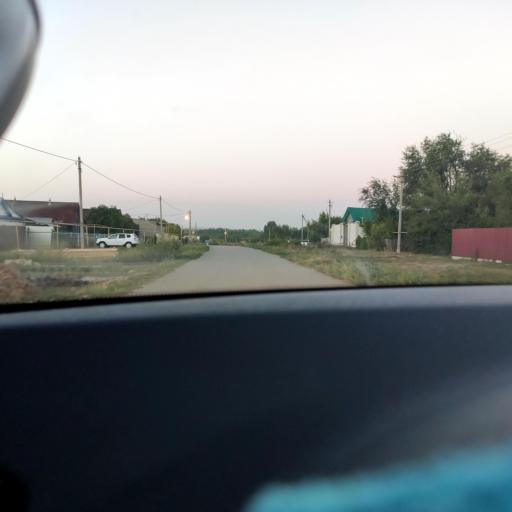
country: RU
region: Samara
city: Novokuybyshevsk
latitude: 53.0761
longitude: 50.0133
